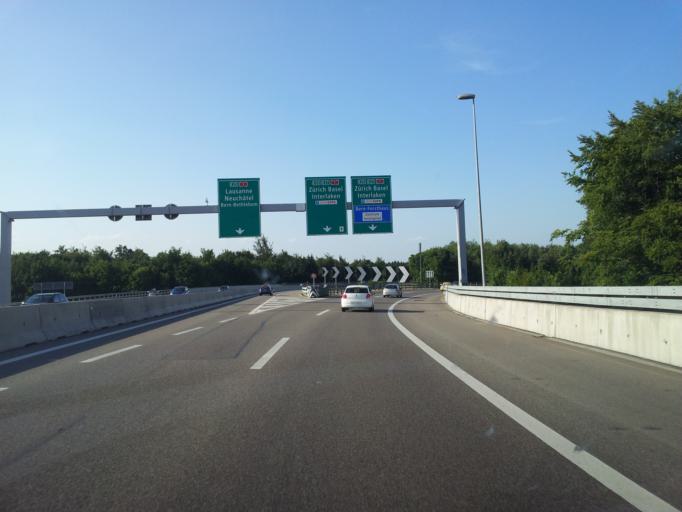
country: CH
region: Bern
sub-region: Bern-Mittelland District
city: Koniz
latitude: 46.9492
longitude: 7.4068
